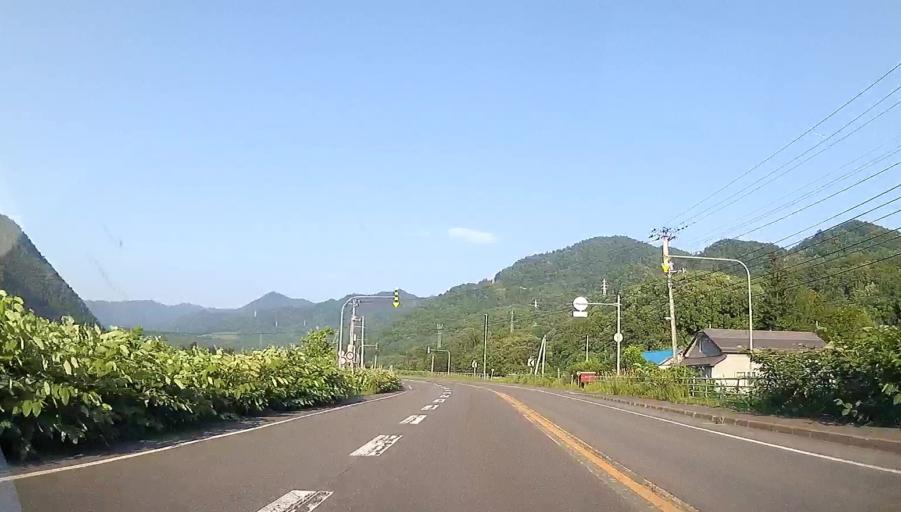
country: JP
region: Hokkaido
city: Shimo-furano
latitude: 42.8916
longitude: 142.5385
